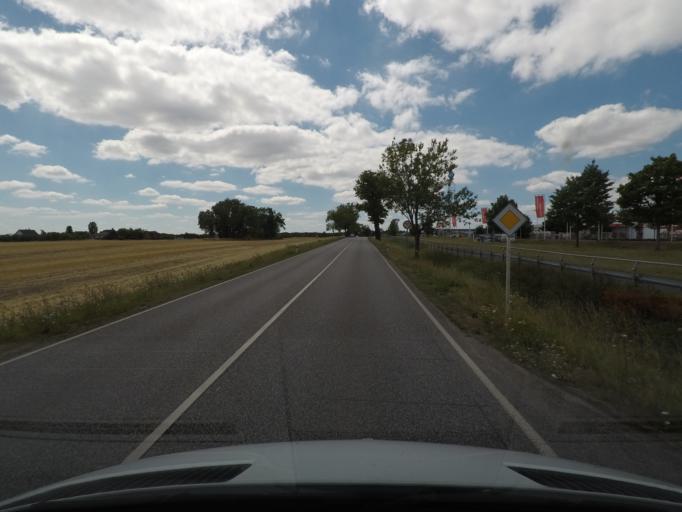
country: DE
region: Brandenburg
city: Ahrensfelde
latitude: 52.5978
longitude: 13.6030
